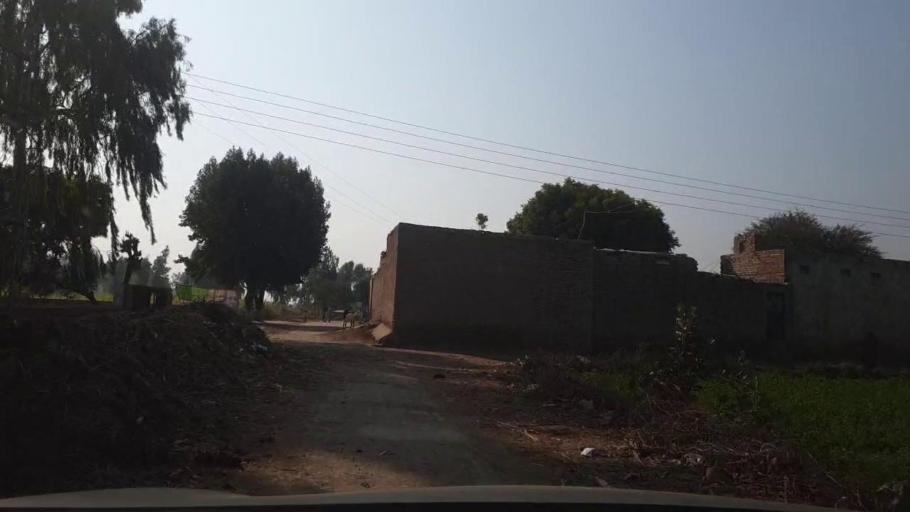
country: PK
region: Sindh
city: Tando Allahyar
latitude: 25.4881
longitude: 68.7565
